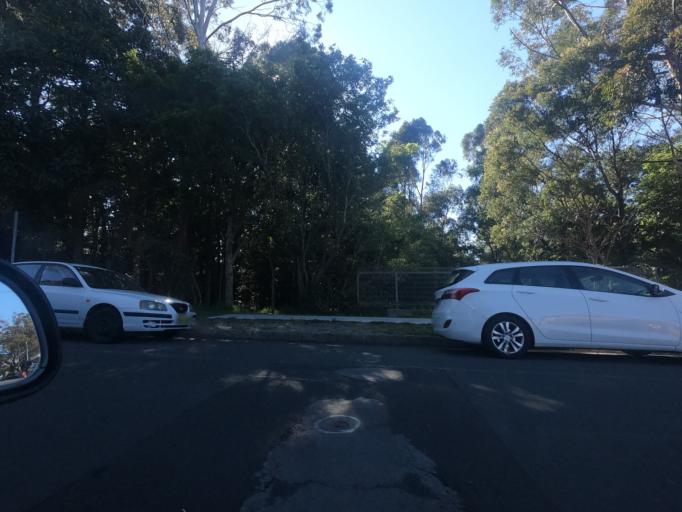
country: AU
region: New South Wales
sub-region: Wollongong
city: Corrimal
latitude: -34.3808
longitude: 150.8880
